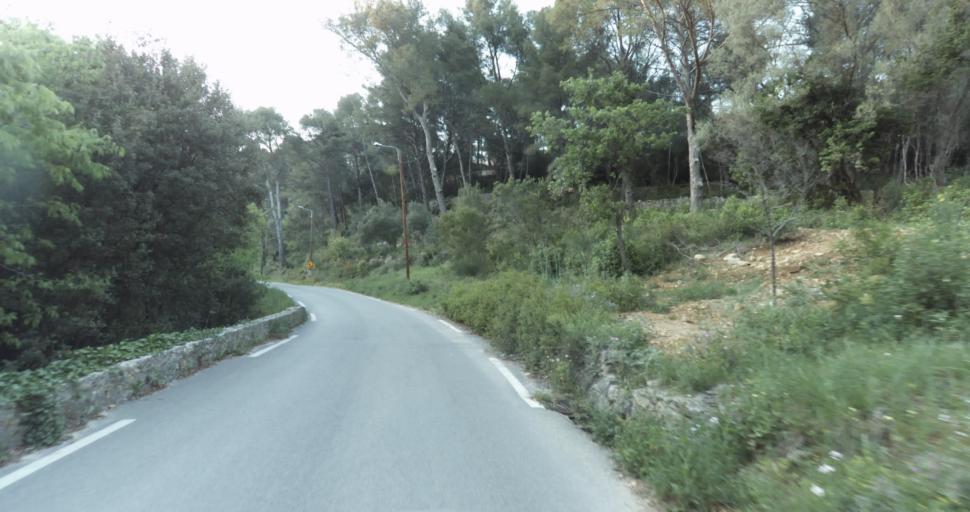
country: FR
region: Provence-Alpes-Cote d'Azur
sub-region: Departement du Var
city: Le Revest-les-Eaux
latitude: 43.1727
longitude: 5.9333
